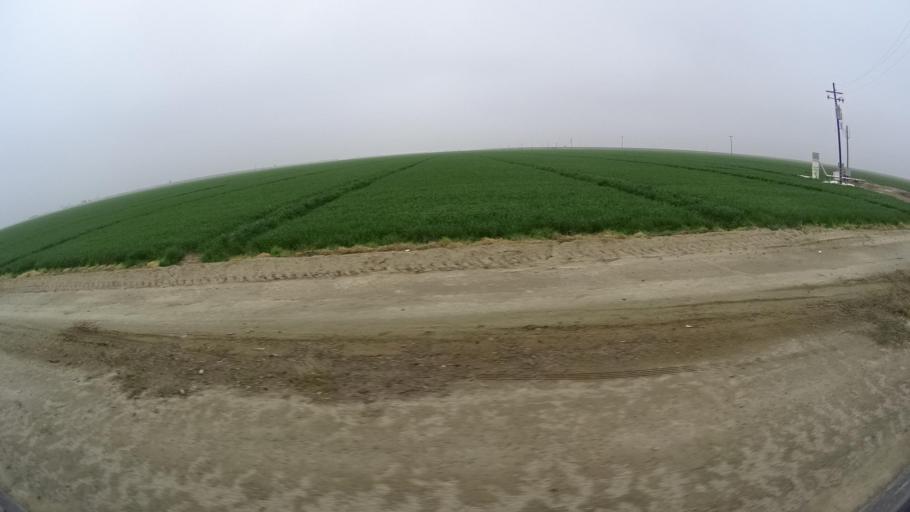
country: US
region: California
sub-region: Kern County
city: Wasco
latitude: 35.7176
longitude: -119.4117
